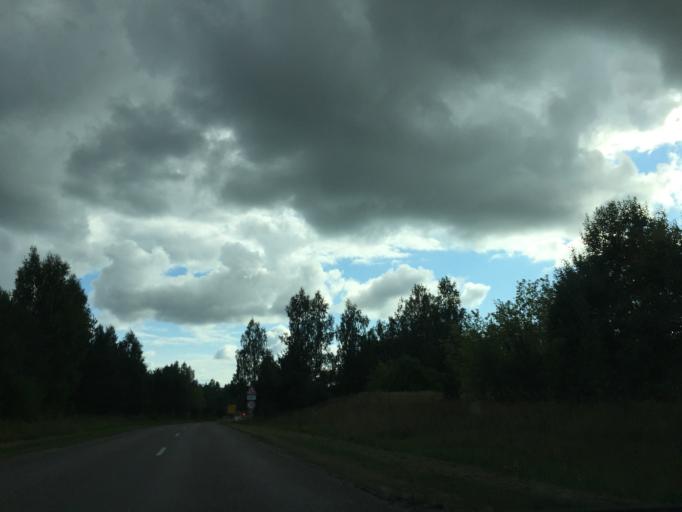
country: LV
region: Limbazu Rajons
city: Limbazi
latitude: 57.3563
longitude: 24.6683
